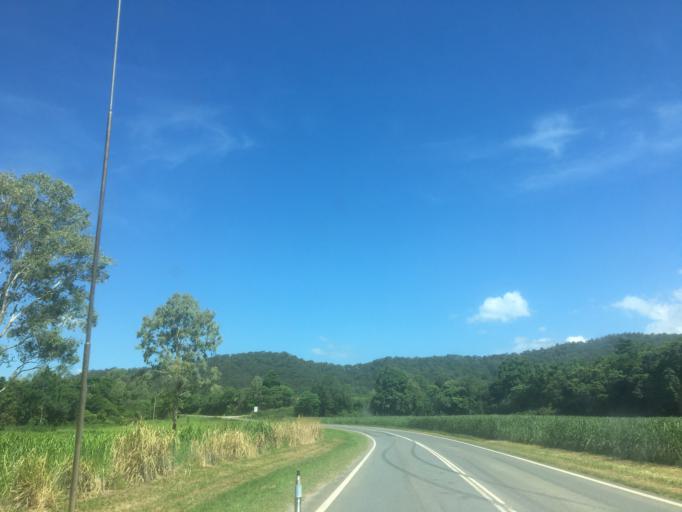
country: AU
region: Queensland
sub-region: Cairns
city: Woree
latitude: -17.0677
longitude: 145.7433
